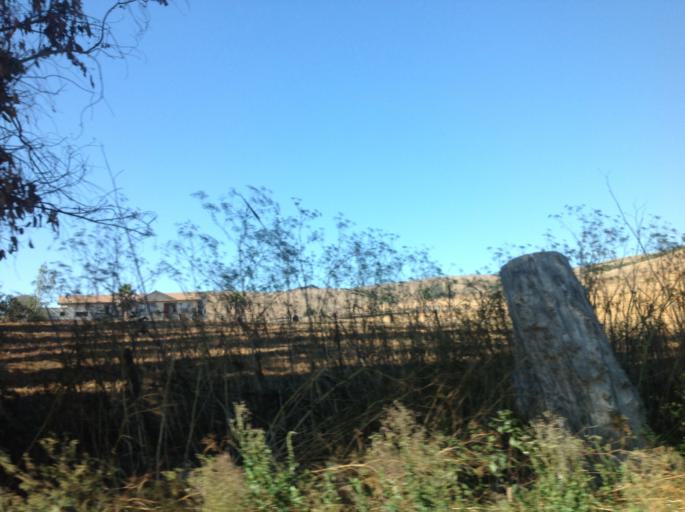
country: US
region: California
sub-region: Sonoma County
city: Occidental
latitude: 38.3213
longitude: -122.9104
